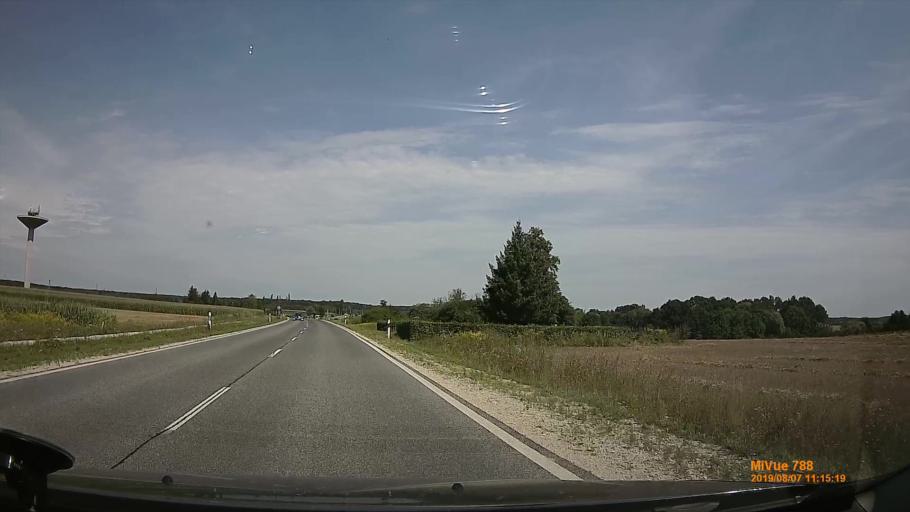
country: HU
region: Zala
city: Lenti
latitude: 46.7146
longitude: 16.5514
